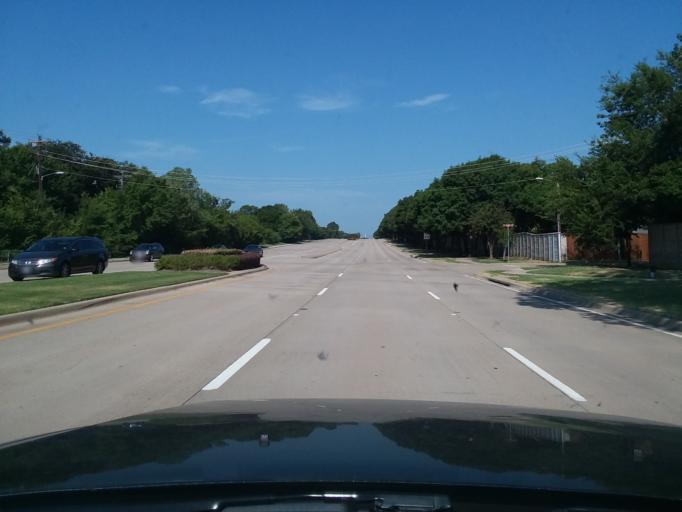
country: US
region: Texas
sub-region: Denton County
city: Flower Mound
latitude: 33.0139
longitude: -97.0555
